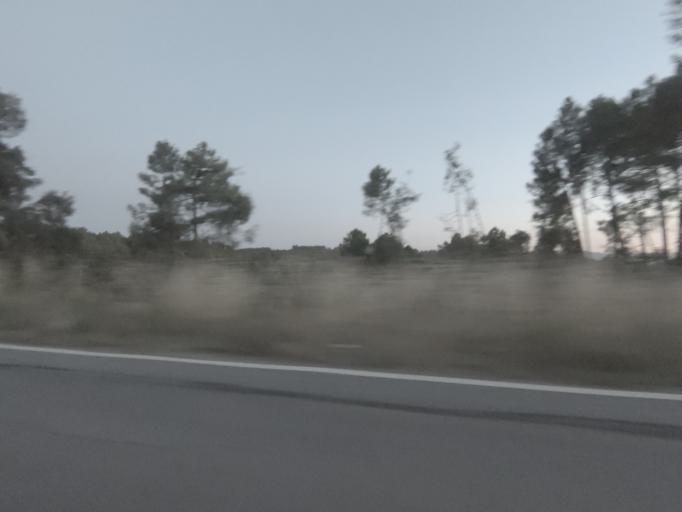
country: PT
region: Vila Real
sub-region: Vila Real
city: Vila Real
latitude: 41.2397
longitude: -7.6867
